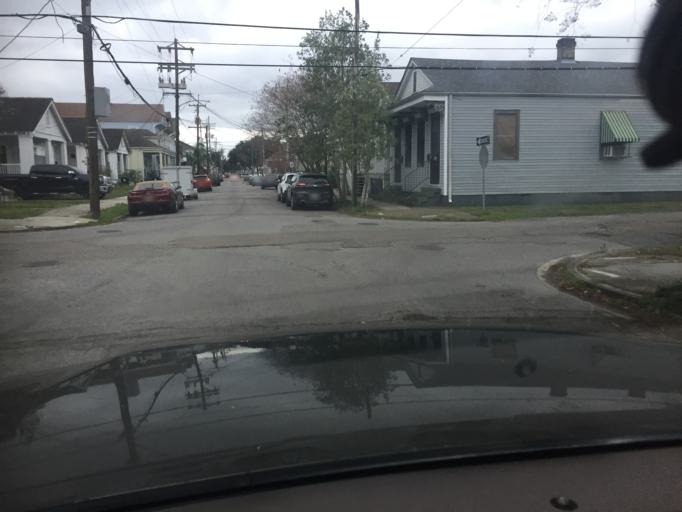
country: US
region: Louisiana
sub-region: Orleans Parish
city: New Orleans
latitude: 29.9741
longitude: -90.0823
